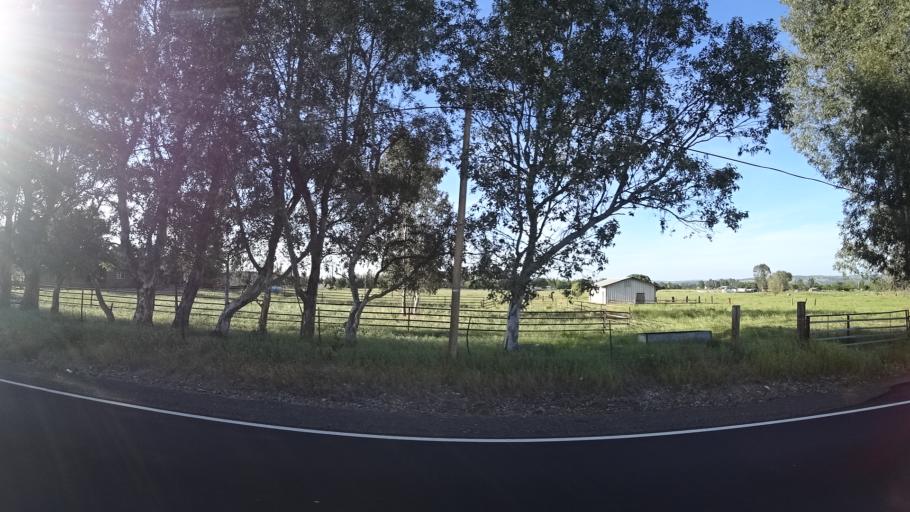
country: US
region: California
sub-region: Placer County
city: Lincoln
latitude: 38.9265
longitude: -121.2924
